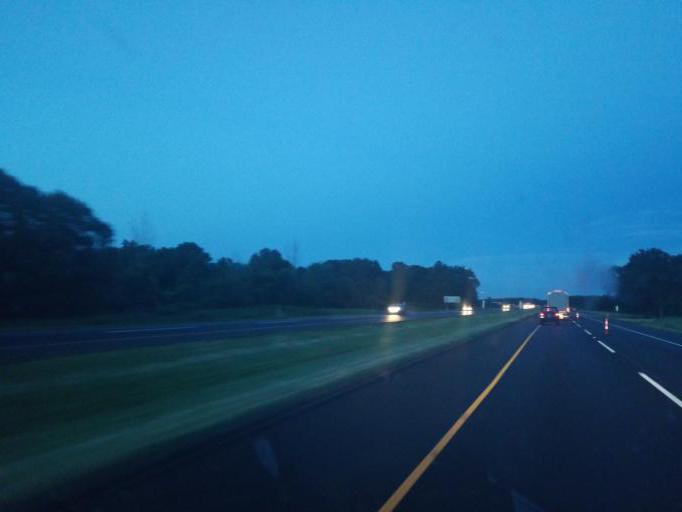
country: US
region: Indiana
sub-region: Saint Joseph County
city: Granger
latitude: 41.7330
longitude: -86.1034
